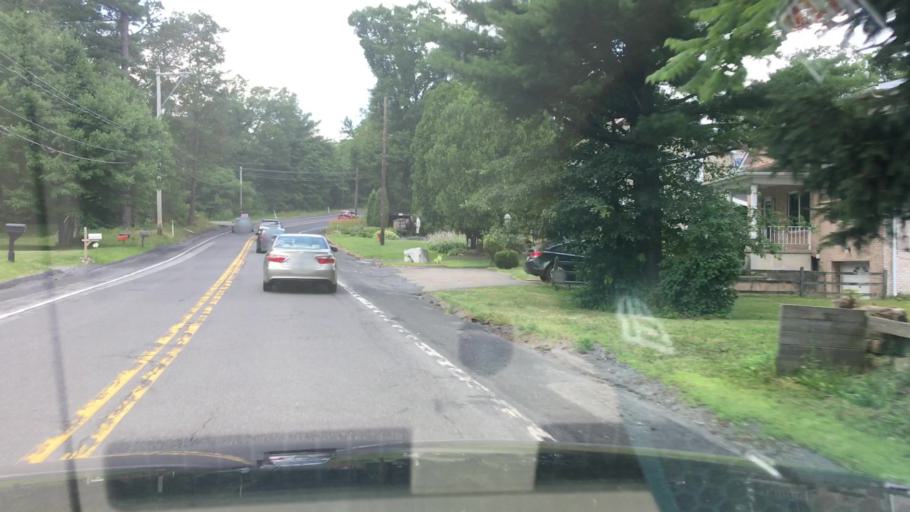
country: US
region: Pennsylvania
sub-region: Schuylkill County
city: Minersville
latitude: 40.7041
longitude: -76.3273
